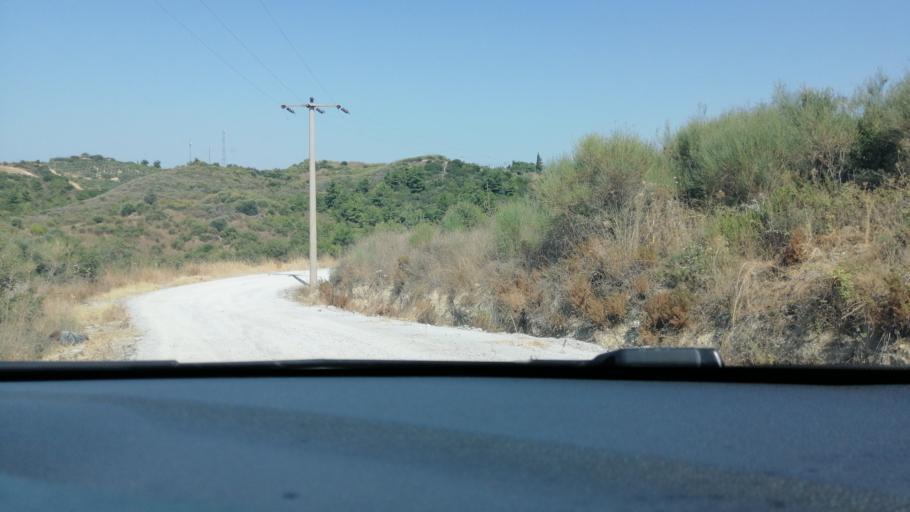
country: TR
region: Aydin
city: Davutlar
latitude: 37.7807
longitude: 27.3134
